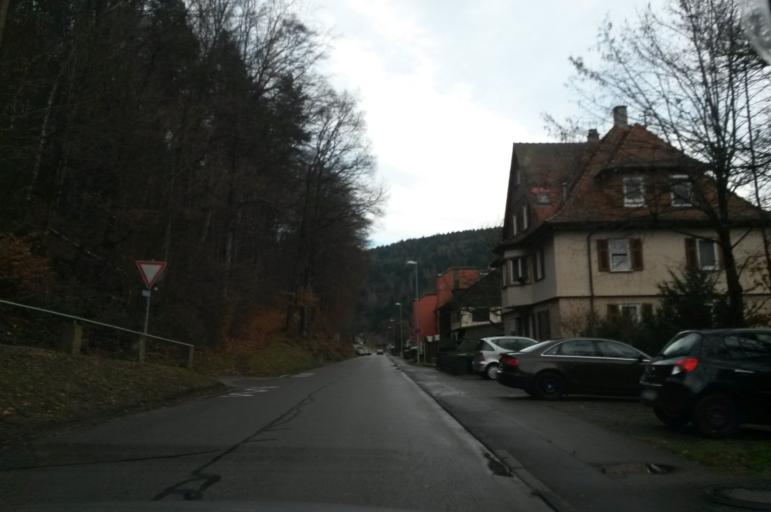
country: DE
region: Baden-Wuerttemberg
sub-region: Karlsruhe Region
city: Neuenburg
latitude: 48.8497
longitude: 8.5947
